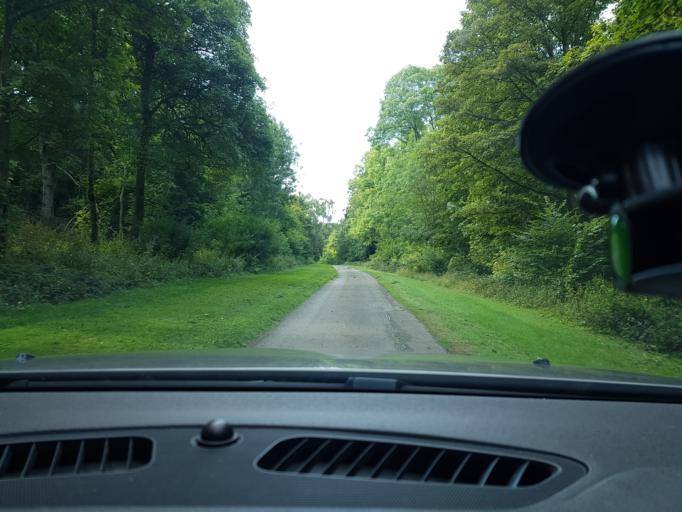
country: GB
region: England
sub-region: West Berkshire
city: Hungerford
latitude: 51.4058
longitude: -1.4834
